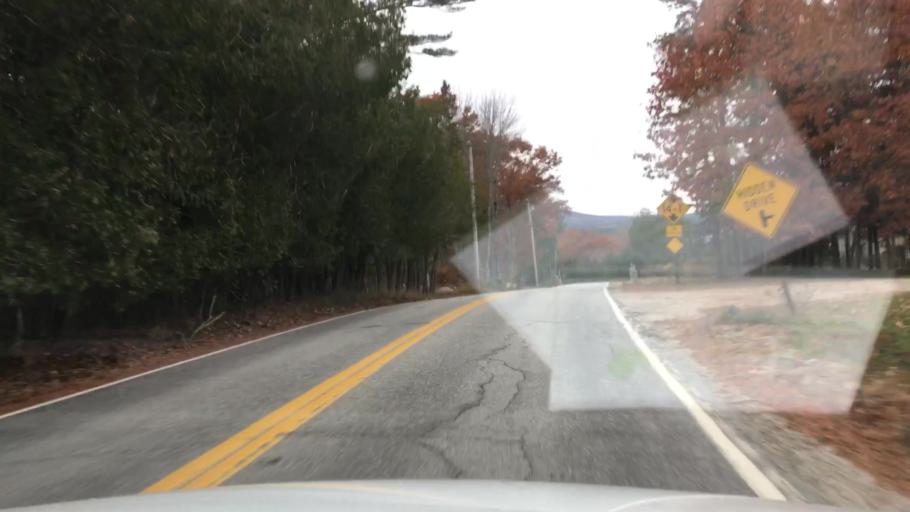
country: US
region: Maine
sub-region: Hancock County
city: Sedgwick
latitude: 44.3710
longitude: -68.5580
